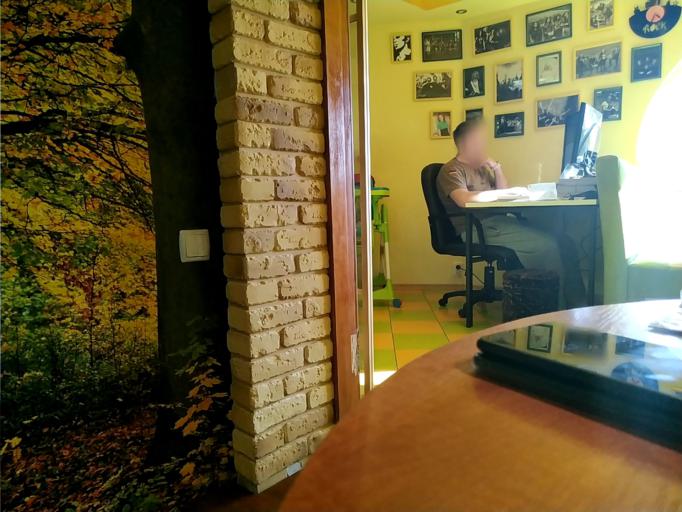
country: RU
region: Vologda
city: Nelazskoye
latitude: 59.4209
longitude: 37.6081
